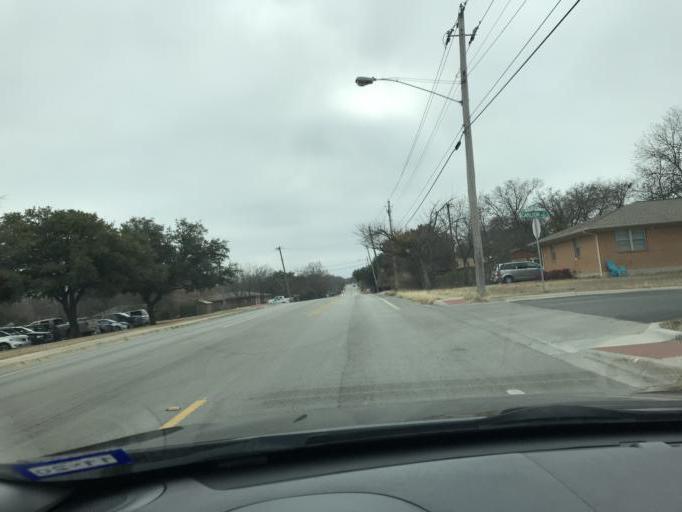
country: US
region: Texas
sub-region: Denton County
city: Denton
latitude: 33.2249
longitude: -97.1498
